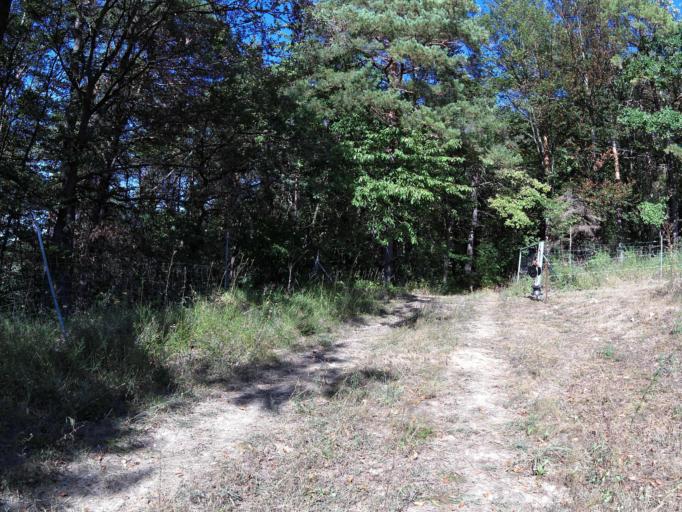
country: DE
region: Bavaria
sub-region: Regierungsbezirk Unterfranken
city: Erlabrunn
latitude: 49.8627
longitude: 9.8616
